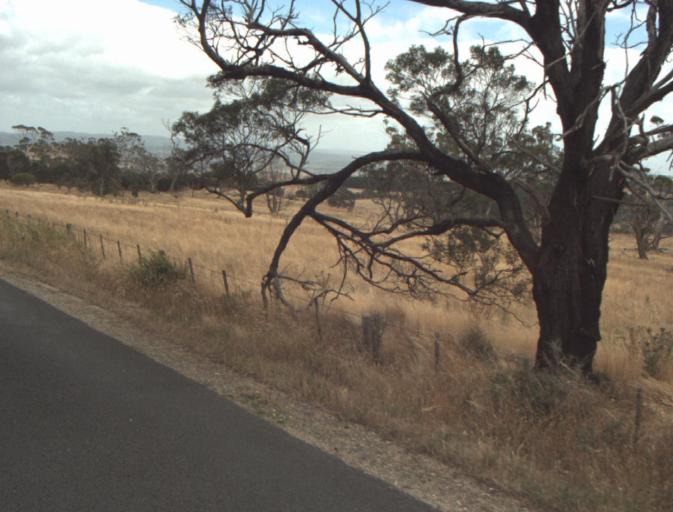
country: AU
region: Tasmania
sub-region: Northern Midlands
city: Evandale
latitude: -41.5130
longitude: 147.3027
